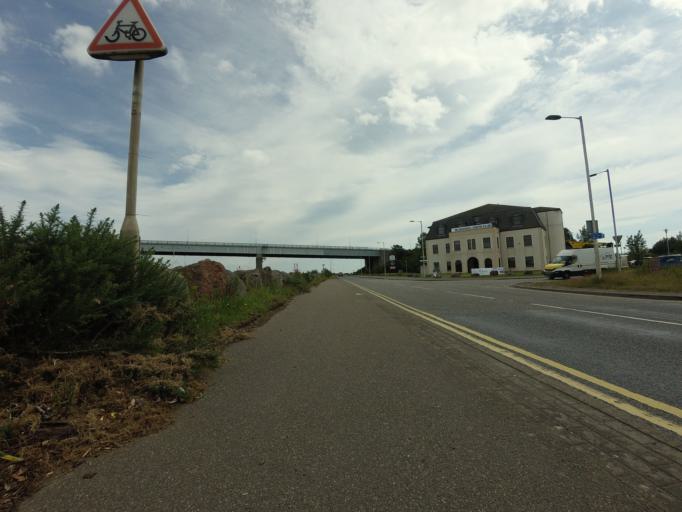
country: GB
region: Scotland
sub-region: Highland
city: Inverness
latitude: 57.4954
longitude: -4.2250
